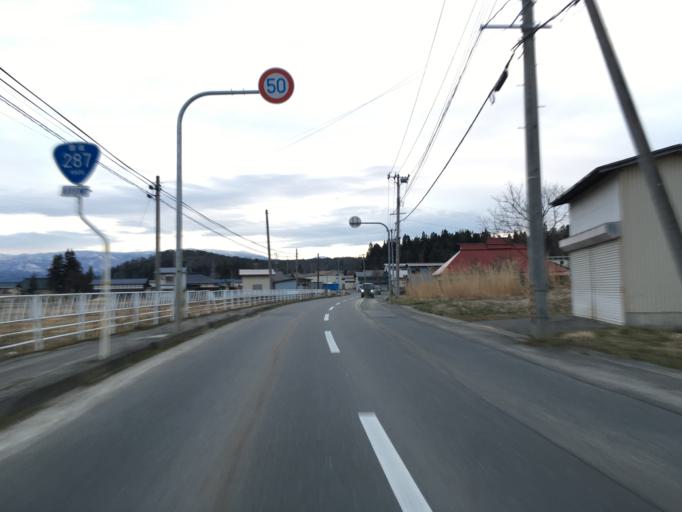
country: JP
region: Yamagata
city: Yonezawa
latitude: 37.9531
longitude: 140.0689
